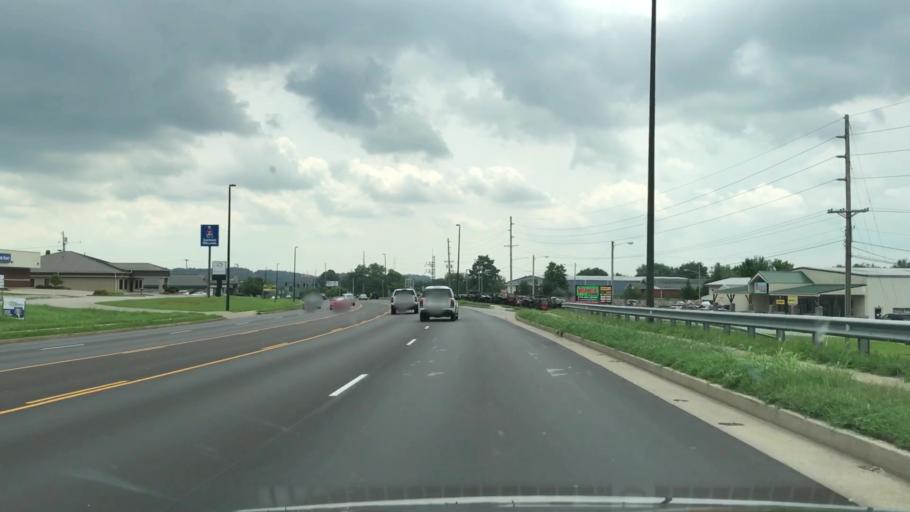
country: US
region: Kentucky
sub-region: Barren County
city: Glasgow
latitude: 36.9927
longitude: -85.9324
